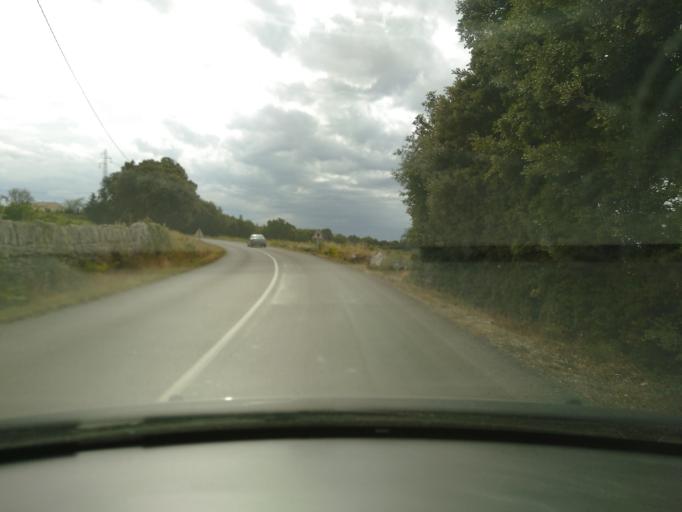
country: FR
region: Rhone-Alpes
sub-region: Departement de la Drome
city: Taulignan
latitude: 44.4433
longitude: 5.0123
